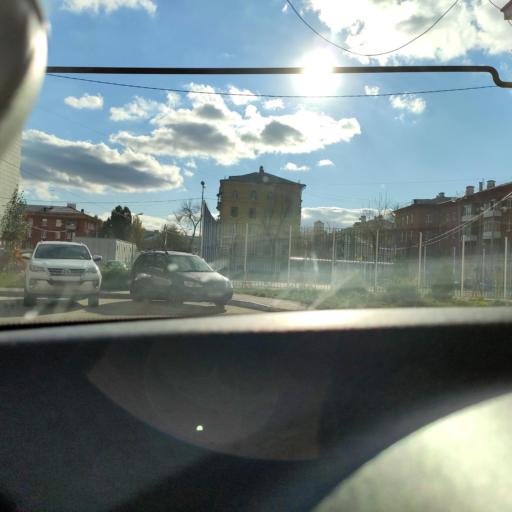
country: RU
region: Samara
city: Petra-Dubrava
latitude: 53.2354
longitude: 50.2788
